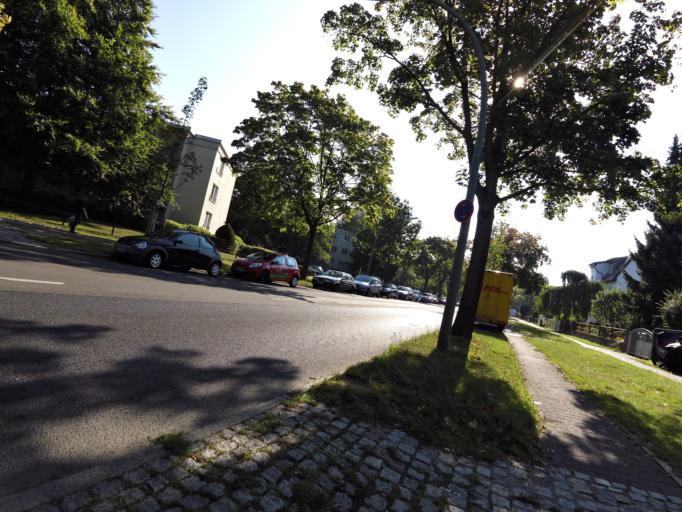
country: DE
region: Berlin
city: Lichtenrade
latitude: 52.3977
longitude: 13.3938
